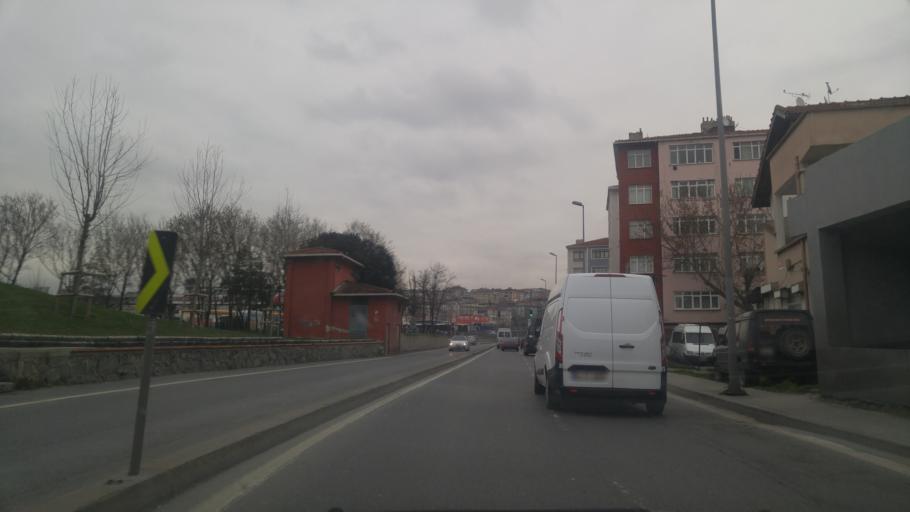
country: TR
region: Istanbul
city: Mahmutbey
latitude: 40.9853
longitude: 28.7688
